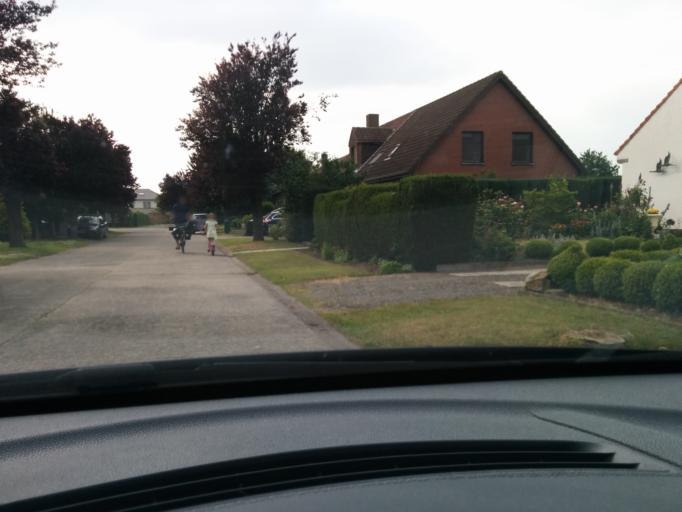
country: BE
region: Flanders
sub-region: Provincie Oost-Vlaanderen
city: De Pinte
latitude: 50.9865
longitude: 3.6691
